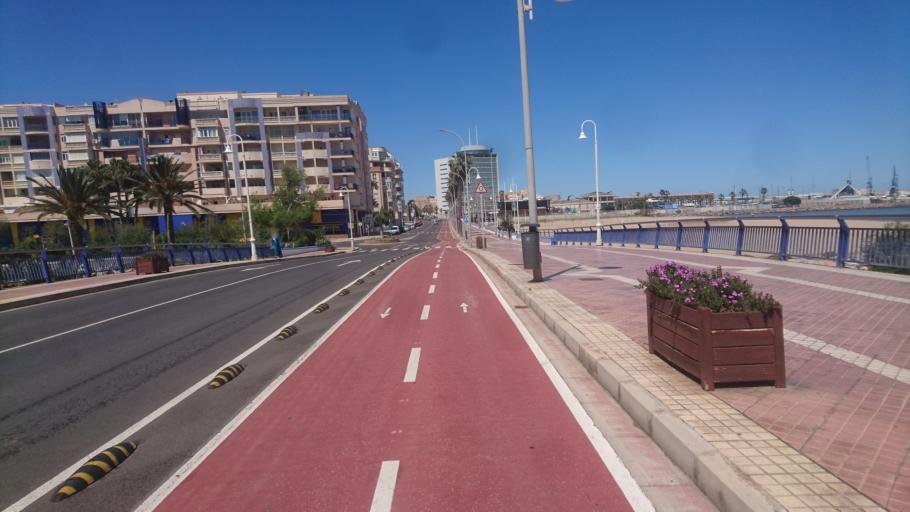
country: ES
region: Melilla
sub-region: Melilla
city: Melilla
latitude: 35.2859
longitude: -2.9385
